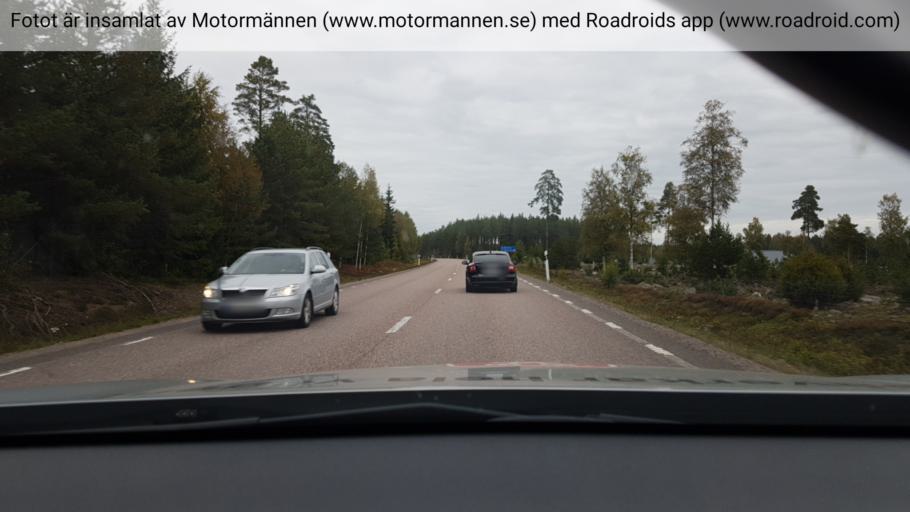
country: SE
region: Gaevleborg
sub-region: Gavle Kommun
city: Hedesunda
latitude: 60.3853
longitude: 16.9748
